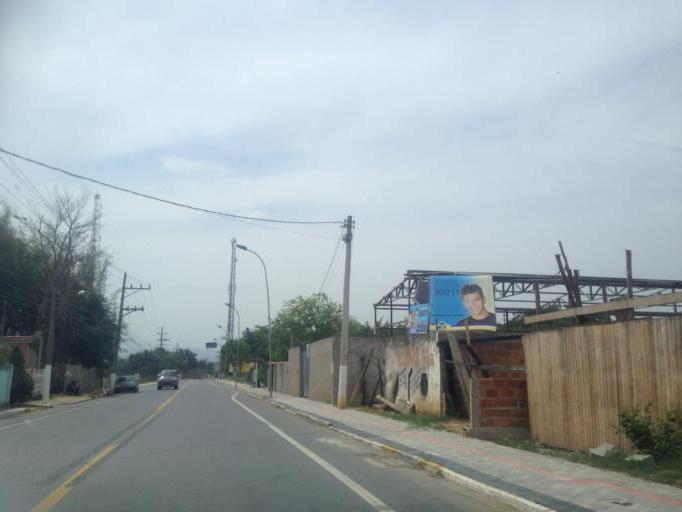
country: BR
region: Rio de Janeiro
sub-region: Porto Real
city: Porto Real
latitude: -22.4493
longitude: -44.3025
